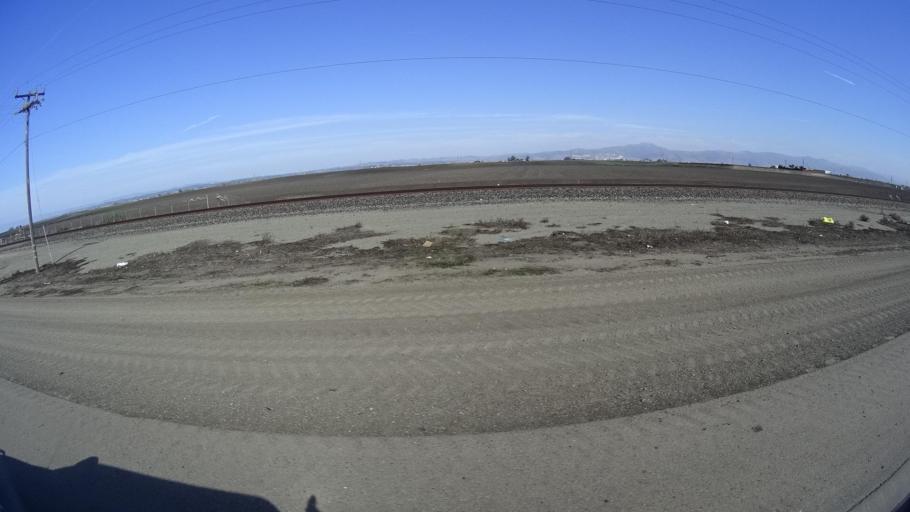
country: US
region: California
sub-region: Monterey County
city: Boronda
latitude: 36.7120
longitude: -121.7157
